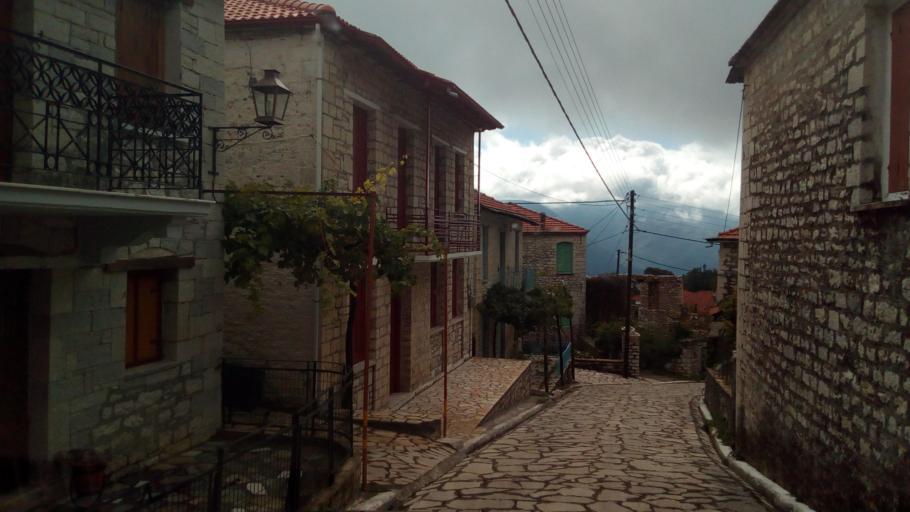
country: GR
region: West Greece
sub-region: Nomos Aitolias kai Akarnanias
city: Thermo
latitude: 38.5989
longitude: 21.7932
